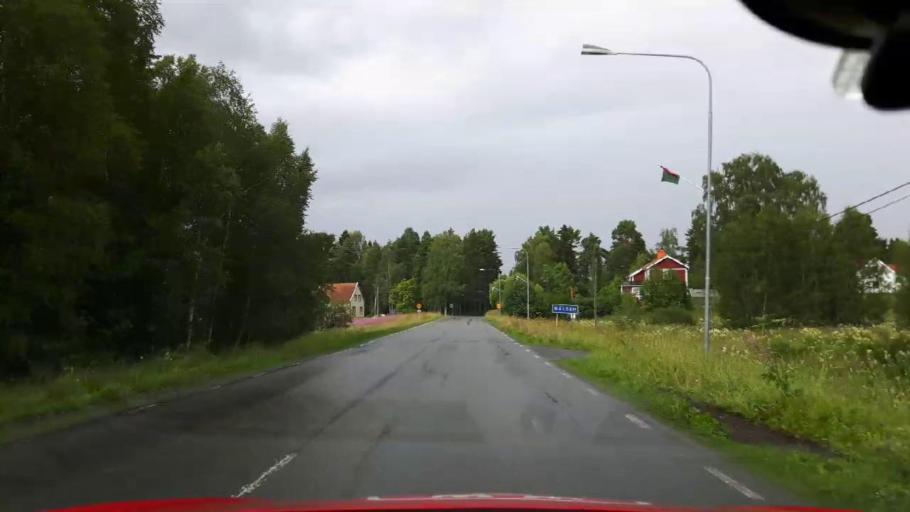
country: SE
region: Jaemtland
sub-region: Krokoms Kommun
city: Krokom
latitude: 63.3457
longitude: 14.2616
